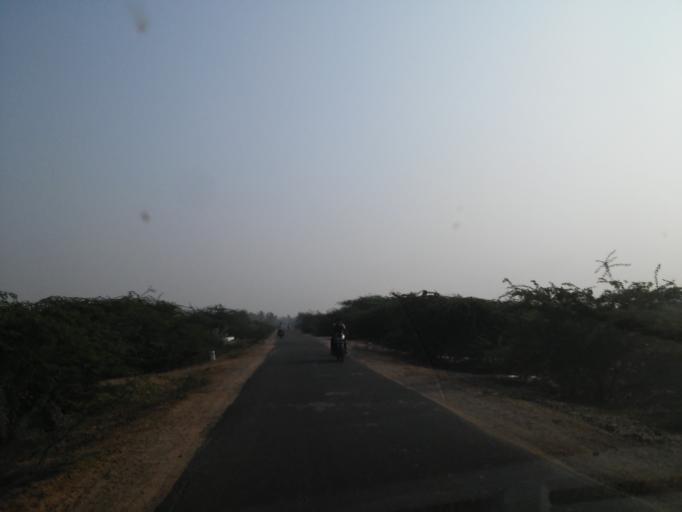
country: IN
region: Gujarat
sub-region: Kachchh
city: Mandvi
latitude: 22.8368
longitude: 69.5238
